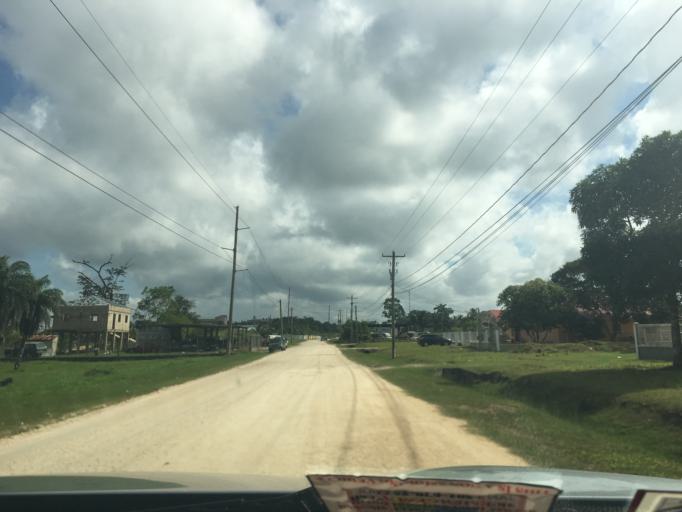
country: BZ
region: Cayo
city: Belmopan
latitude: 17.2509
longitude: -88.7898
